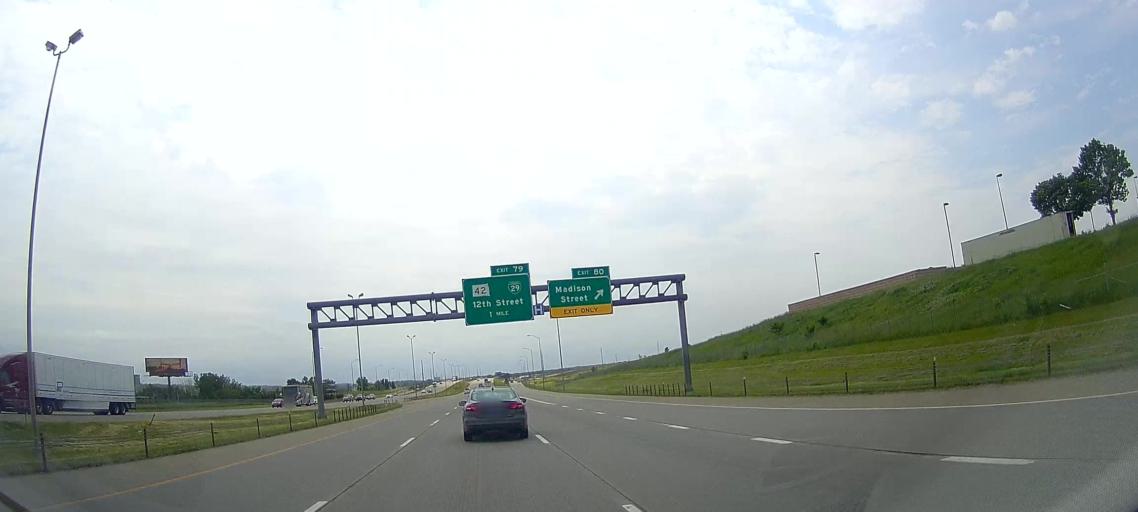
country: US
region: South Dakota
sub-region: Minnehaha County
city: Sioux Falls
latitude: 43.5650
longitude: -96.7788
